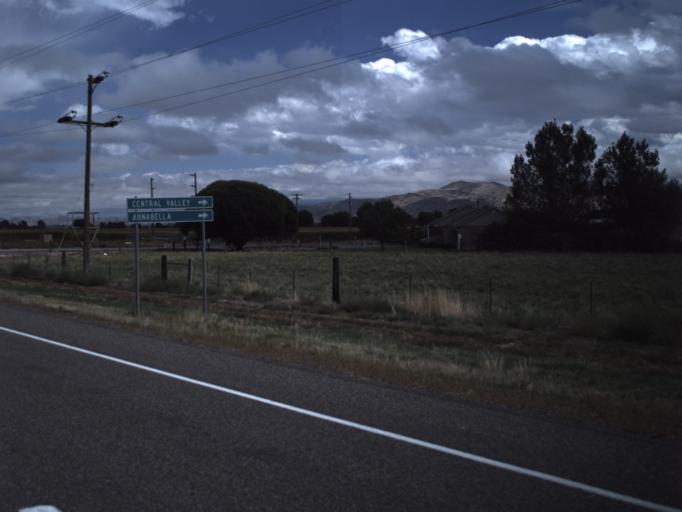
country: US
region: Utah
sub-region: Sevier County
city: Monroe
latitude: 38.7023
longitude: -112.1106
